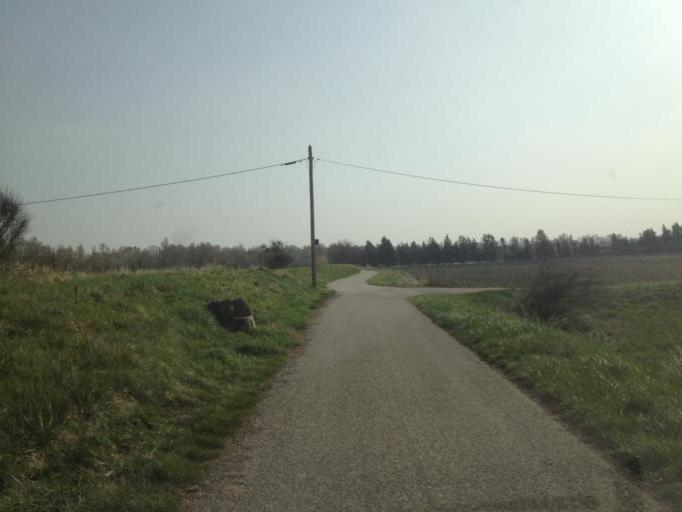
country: FR
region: Provence-Alpes-Cote d'Azur
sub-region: Departement du Vaucluse
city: Bedarrides
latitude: 44.0481
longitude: 4.9284
